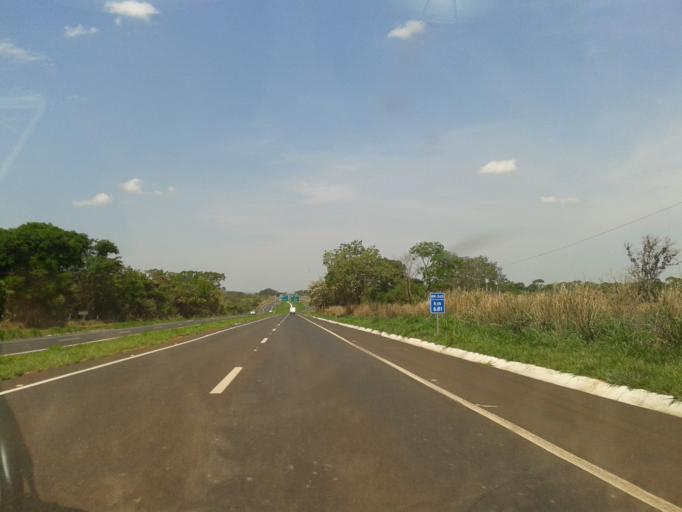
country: BR
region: Minas Gerais
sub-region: Monte Alegre De Minas
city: Monte Alegre de Minas
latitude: -18.8506
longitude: -48.8038
